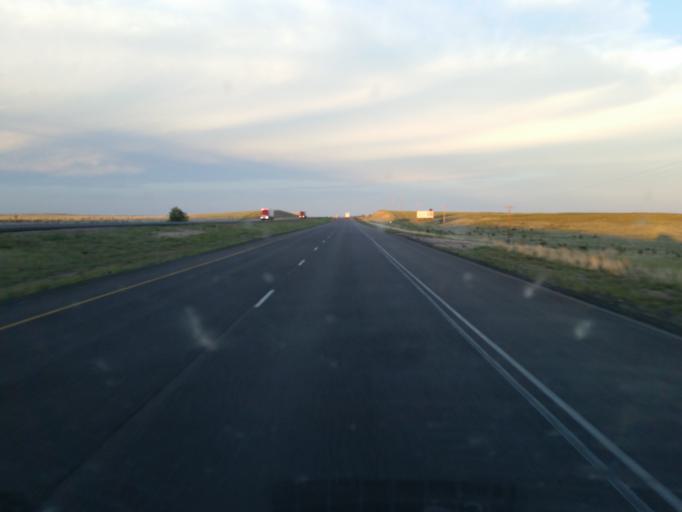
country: US
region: New Mexico
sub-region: Guadalupe County
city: Santa Rosa
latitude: 34.9901
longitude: -105.2682
